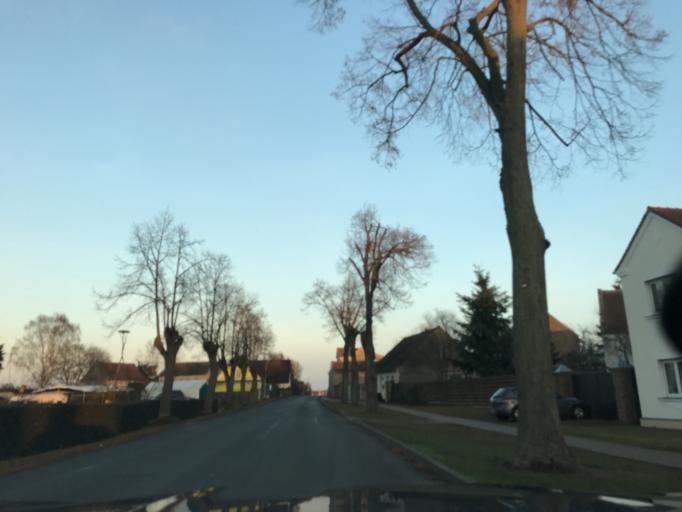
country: DE
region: Brandenburg
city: Wusterwitz
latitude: 52.4744
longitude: 12.4549
